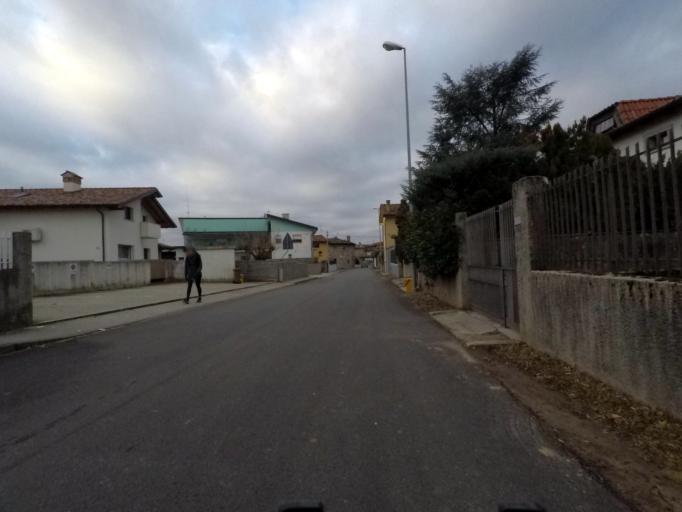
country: IT
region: Friuli Venezia Giulia
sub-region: Provincia di Udine
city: Colugna
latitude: 46.0911
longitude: 13.2048
